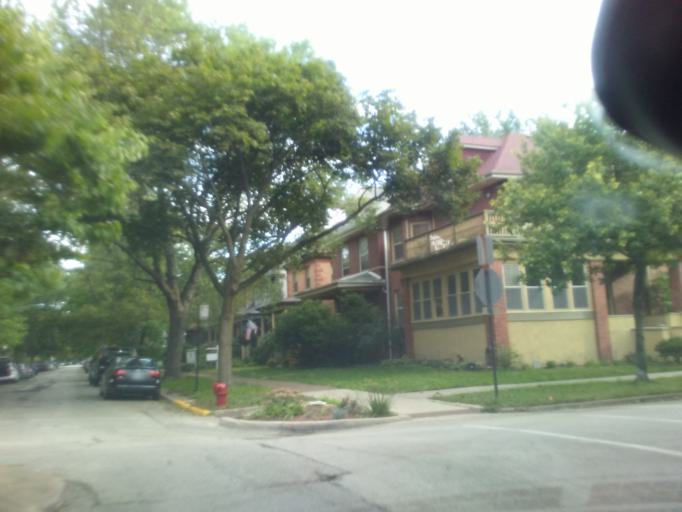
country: US
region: Illinois
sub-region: Cook County
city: Evanston
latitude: 41.9781
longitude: -87.6624
